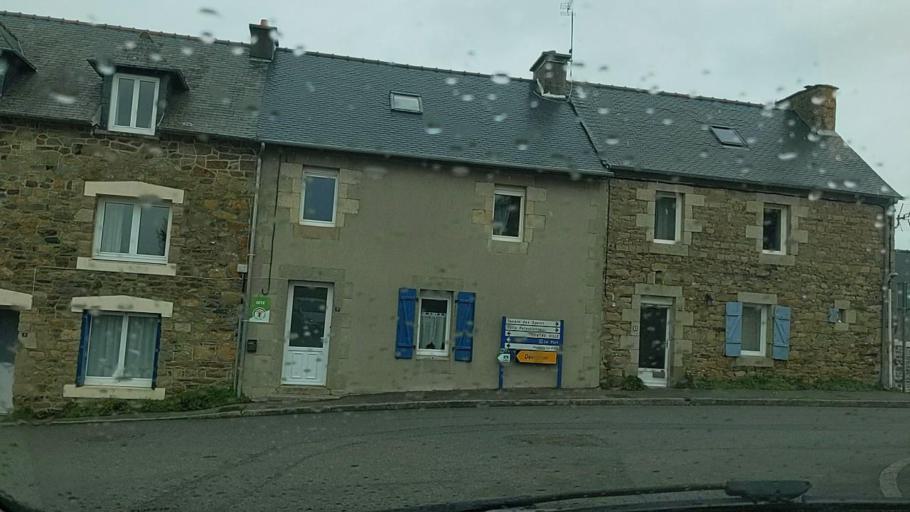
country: FR
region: Brittany
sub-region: Departement des Cotes-d'Armor
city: Lezardrieux
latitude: 48.7864
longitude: -3.1038
